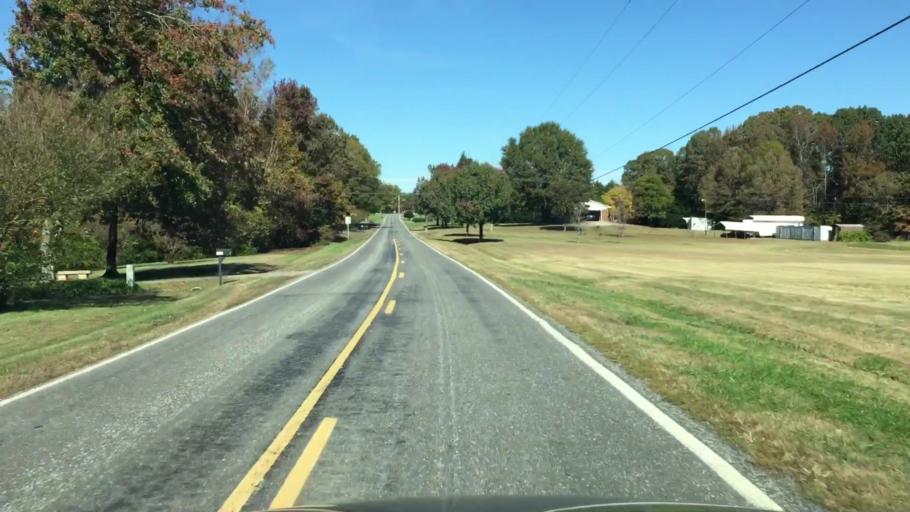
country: US
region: North Carolina
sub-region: Iredell County
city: Mooresville
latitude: 35.5807
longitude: -80.7616
